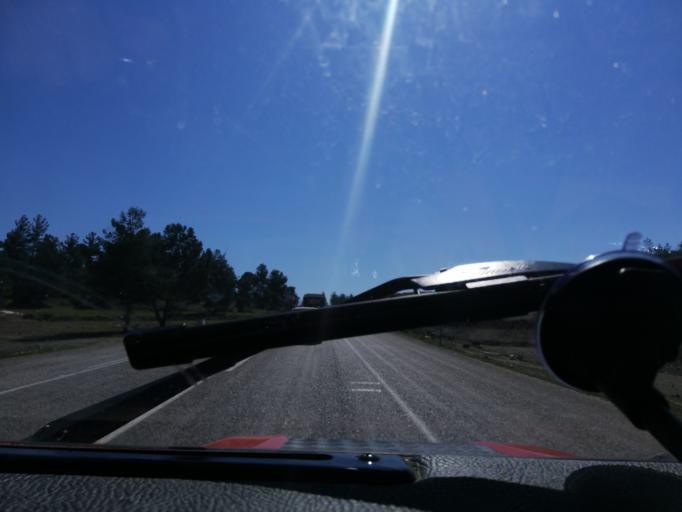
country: TR
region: Mugla
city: Kemer
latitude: 36.6120
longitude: 29.3581
